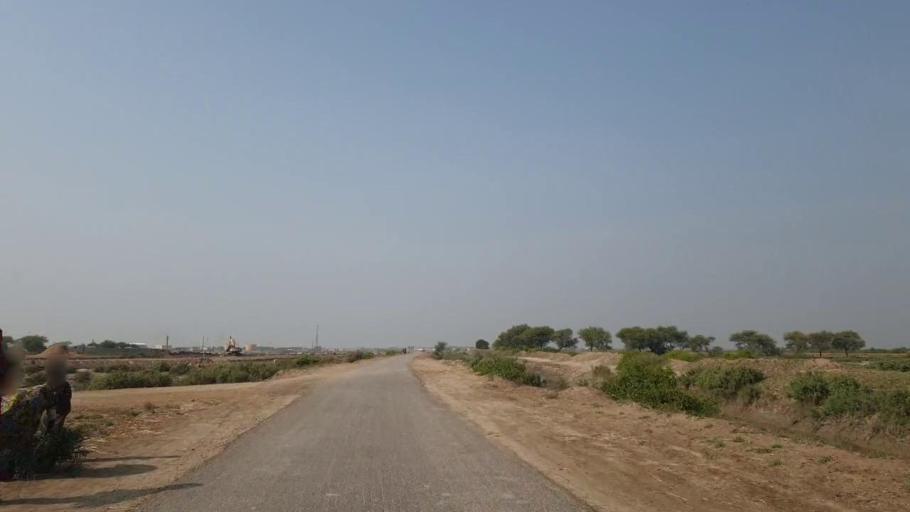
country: PK
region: Sindh
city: Matli
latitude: 24.9620
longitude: 68.5172
